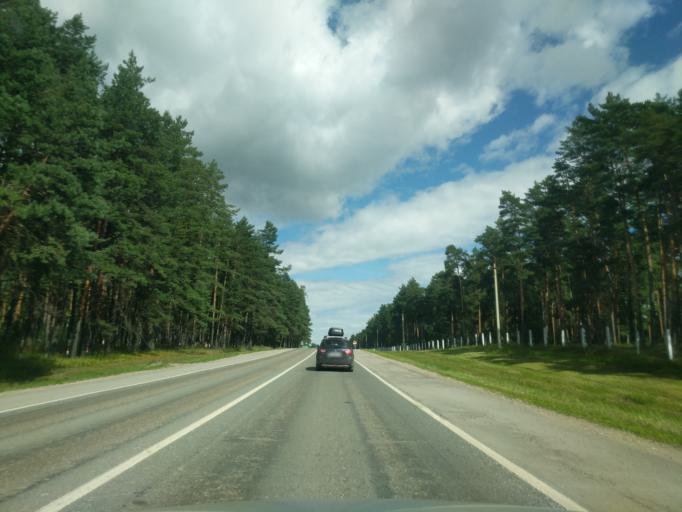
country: RU
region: Jaroslavl
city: Levashevo
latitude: 57.6737
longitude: 40.5848
